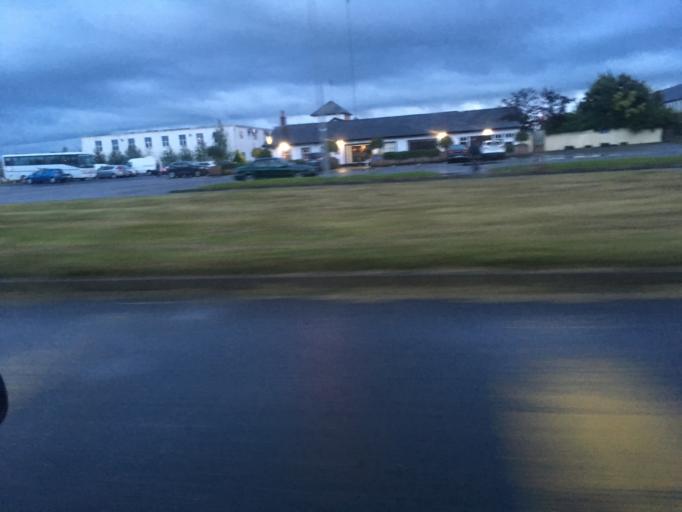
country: IE
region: Leinster
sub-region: Kildare
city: Droichead Nua
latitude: 53.2075
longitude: -6.7443
